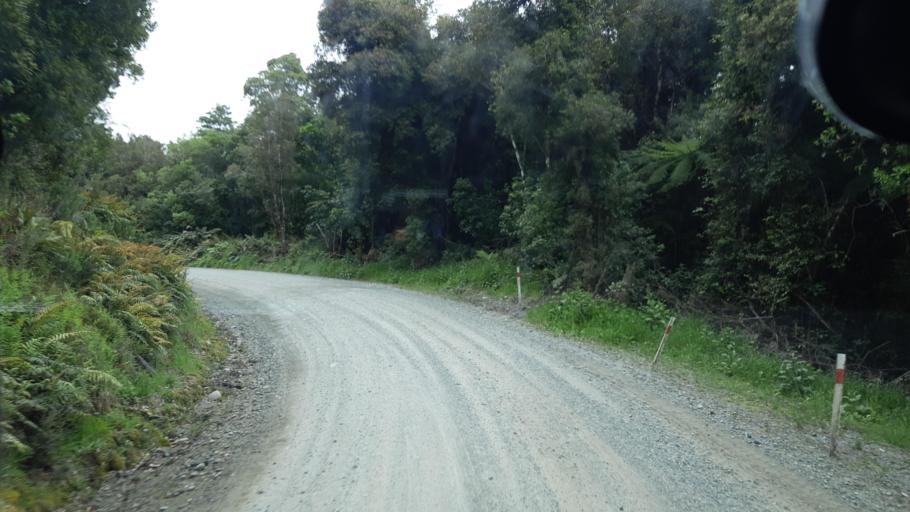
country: NZ
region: West Coast
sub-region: Grey District
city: Greymouth
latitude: -42.6369
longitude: 171.3811
